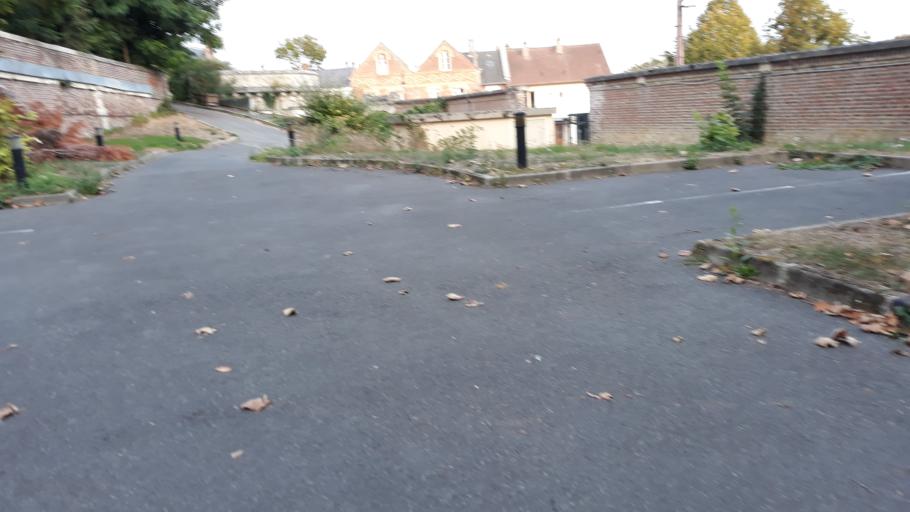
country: FR
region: Picardie
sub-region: Departement de l'Aisne
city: Laon
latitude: 49.5602
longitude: 3.6117
